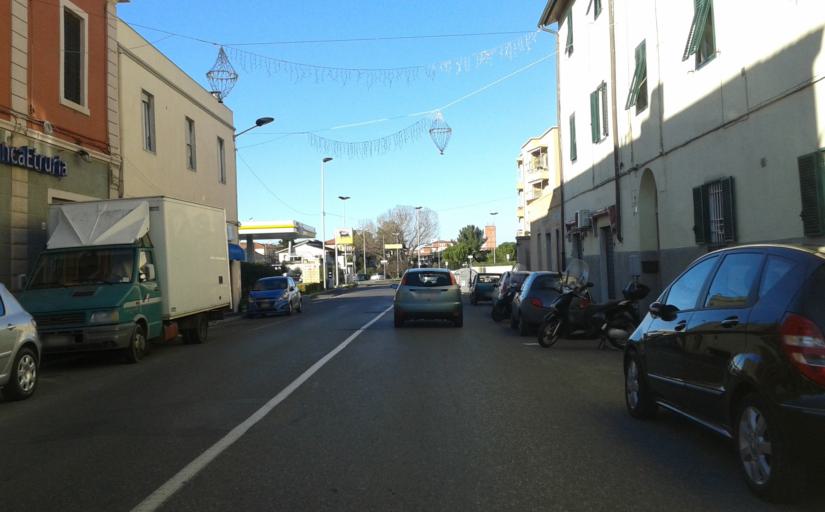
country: IT
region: Tuscany
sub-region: Provincia di Livorno
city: Livorno
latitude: 43.5184
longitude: 10.3244
